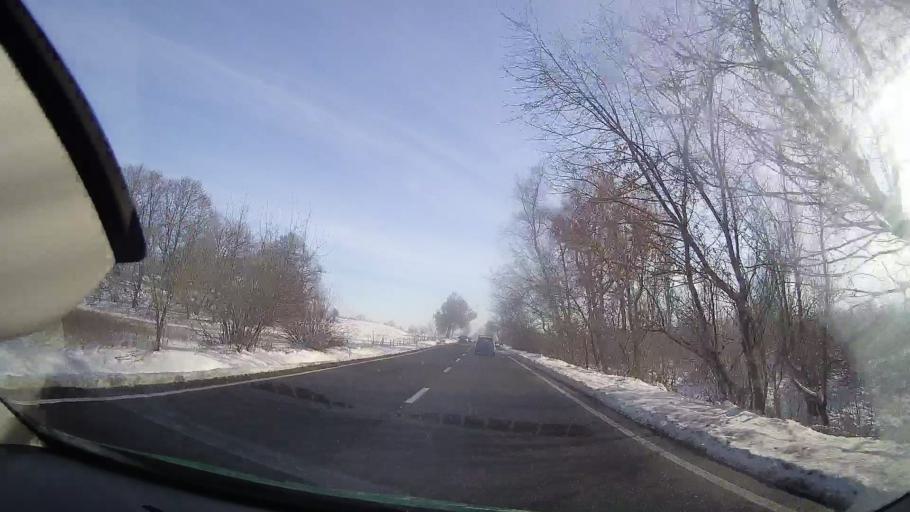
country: RO
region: Neamt
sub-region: Comuna Negresti
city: Negresti
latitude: 47.0692
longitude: 26.3675
